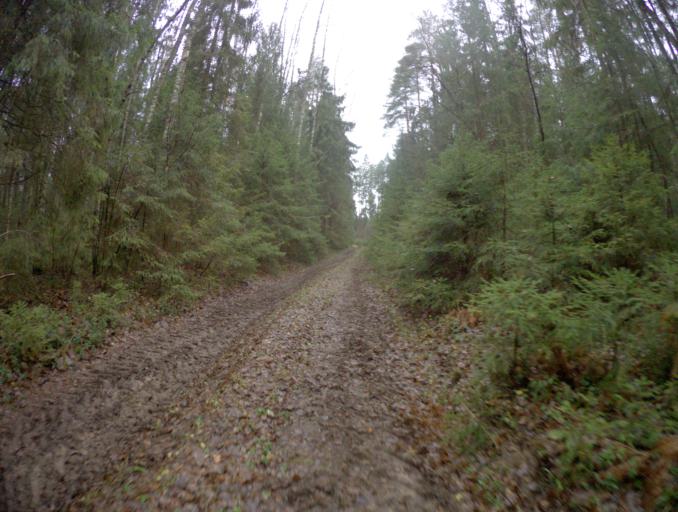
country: RU
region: Vladimir
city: Golovino
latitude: 56.0038
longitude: 40.4725
